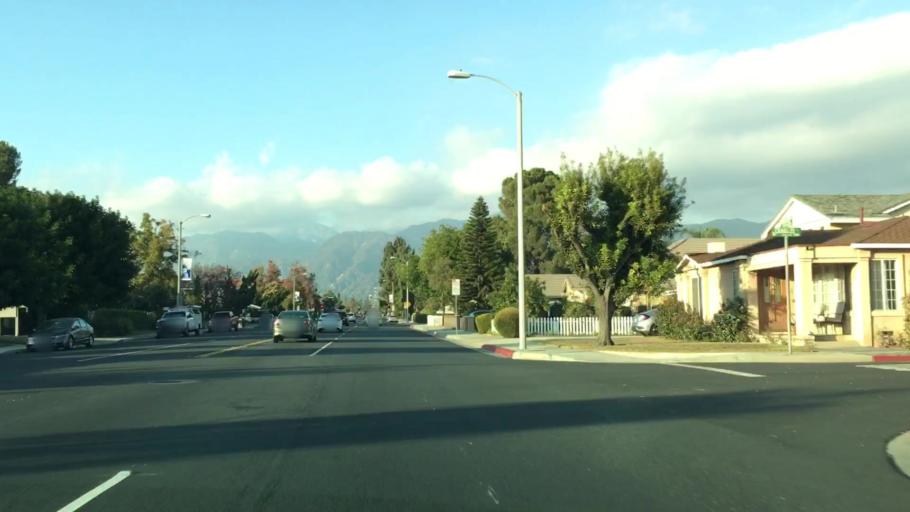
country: US
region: California
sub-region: Los Angeles County
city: Temple City
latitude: 34.1146
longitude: -118.0624
